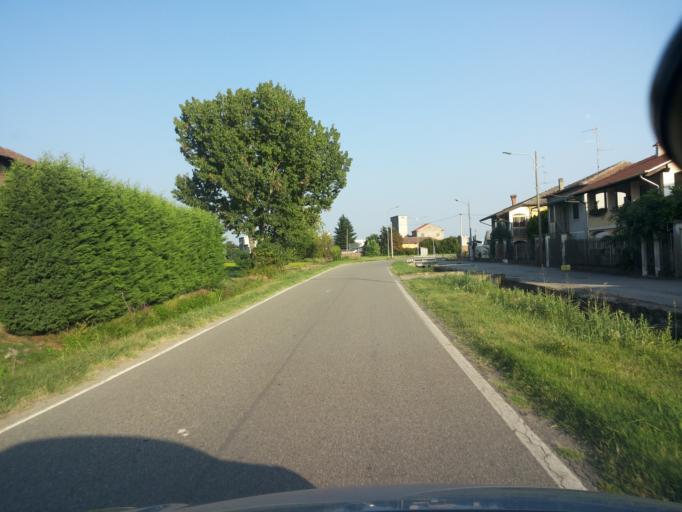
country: IT
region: Piedmont
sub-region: Provincia di Vercelli
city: Sali Vercellese
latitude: 45.3084
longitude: 8.3293
